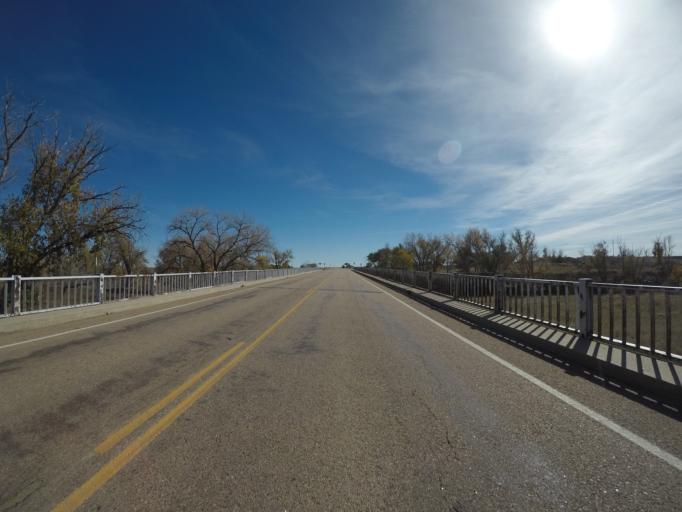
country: US
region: Colorado
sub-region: Yuma County
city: Yuma
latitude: 39.6577
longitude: -102.8464
